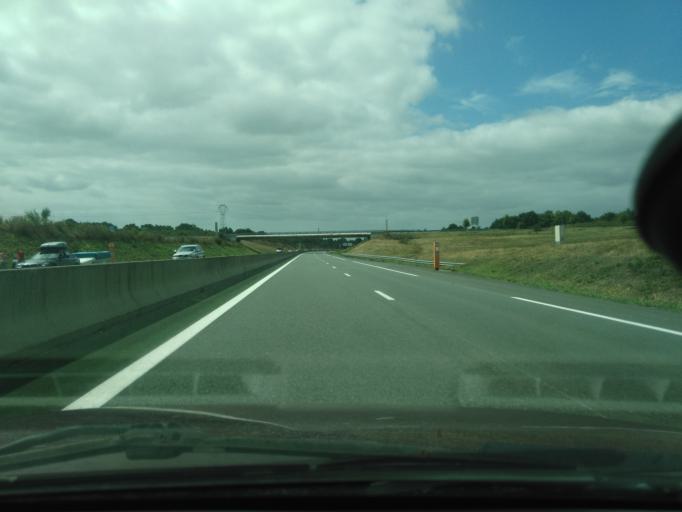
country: FR
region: Pays de la Loire
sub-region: Departement de la Vendee
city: La Roche-sur-Yon
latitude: 46.6391
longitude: -1.3973
